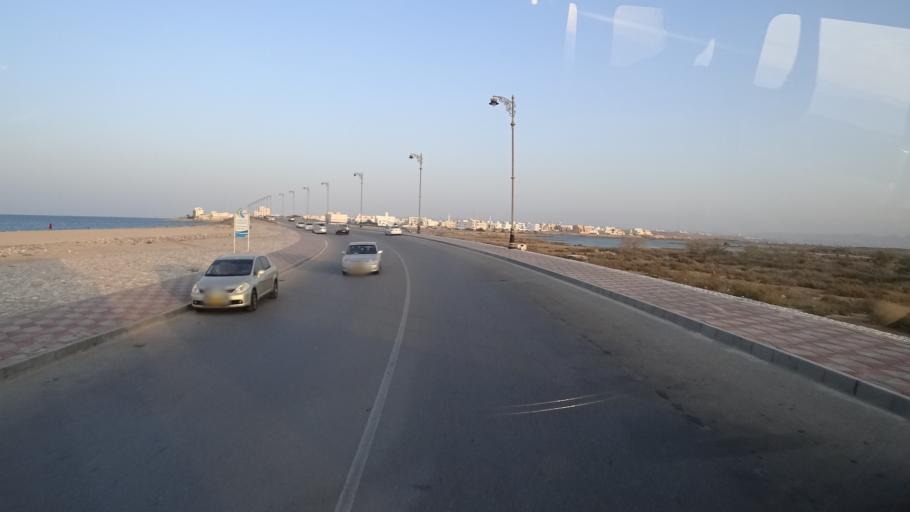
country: OM
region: Ash Sharqiyah
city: Sur
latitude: 22.5988
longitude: 59.4860
